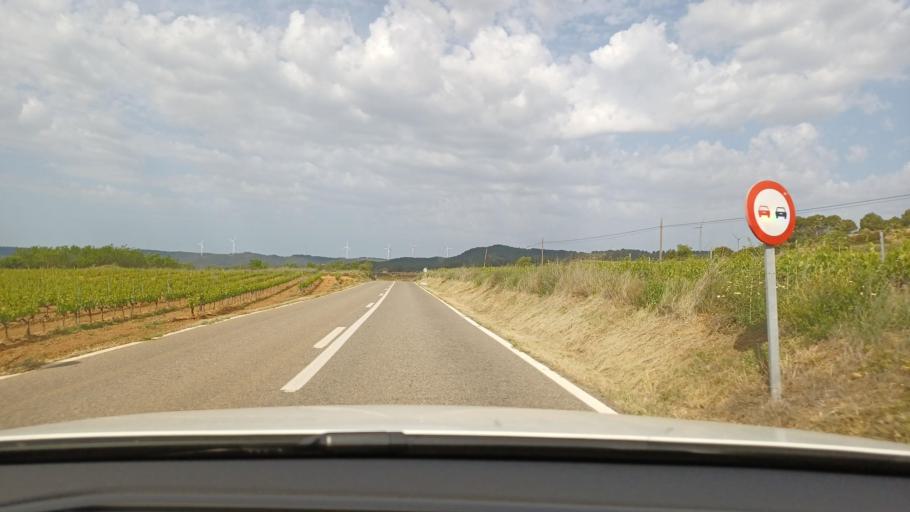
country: ES
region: Catalonia
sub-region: Provincia de Tarragona
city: Bot
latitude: 41.0430
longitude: 0.3931
